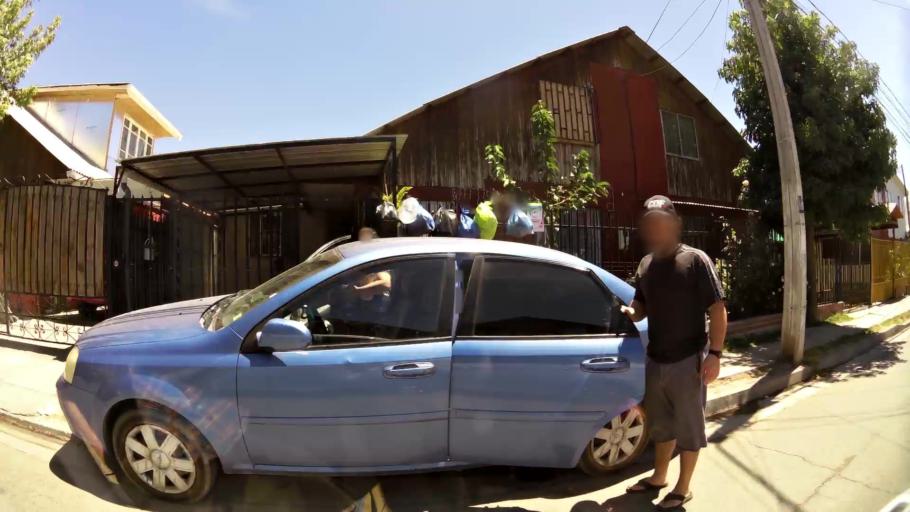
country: CL
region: O'Higgins
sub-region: Provincia de Cachapoal
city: Rancagua
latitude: -34.1568
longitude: -70.7557
